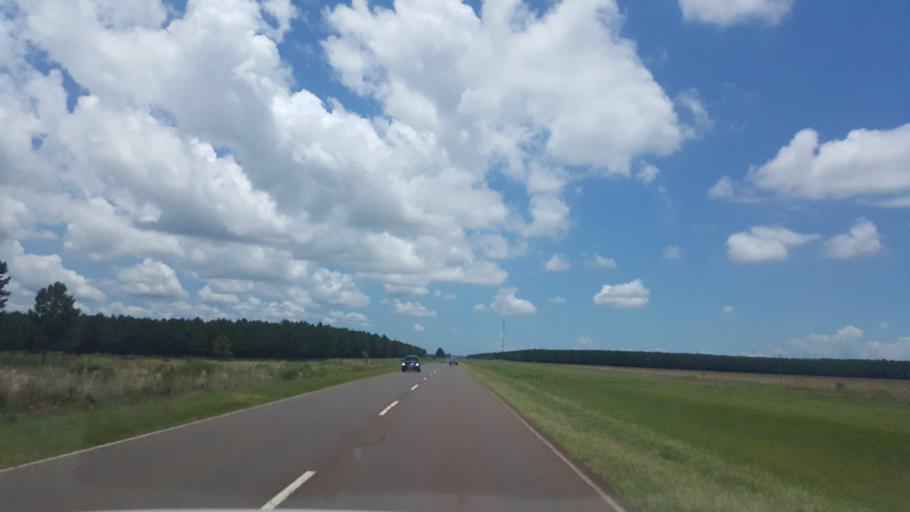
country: PY
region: Itapua
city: San Juan del Parana
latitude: -27.5146
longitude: -56.1446
